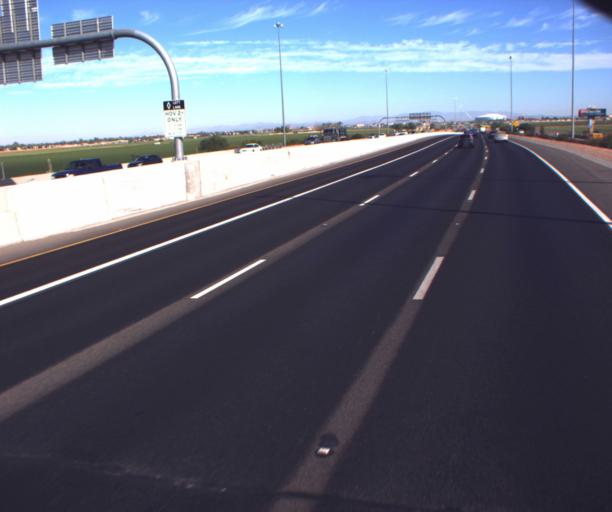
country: US
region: Arizona
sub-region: Maricopa County
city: Tolleson
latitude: 33.4798
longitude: -112.2637
